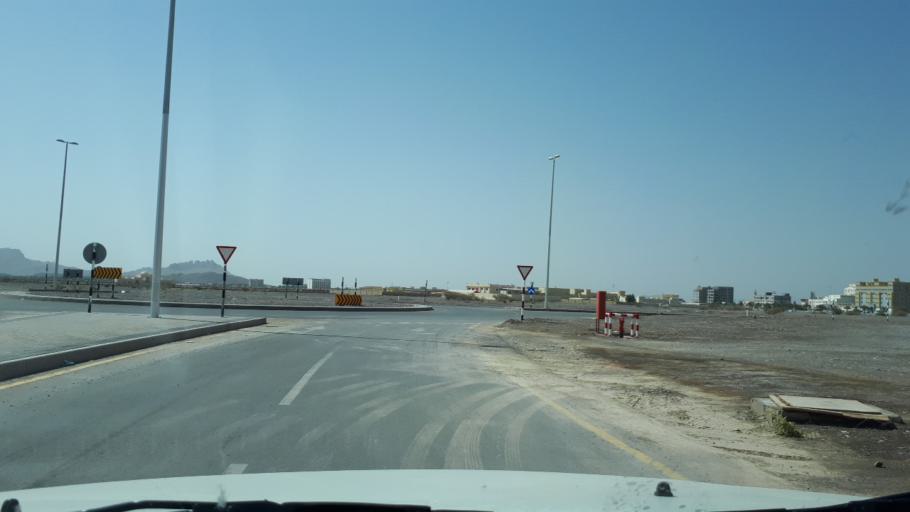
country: OM
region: Muhafazat ad Dakhiliyah
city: Nizwa
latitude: 22.8713
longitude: 57.5393
